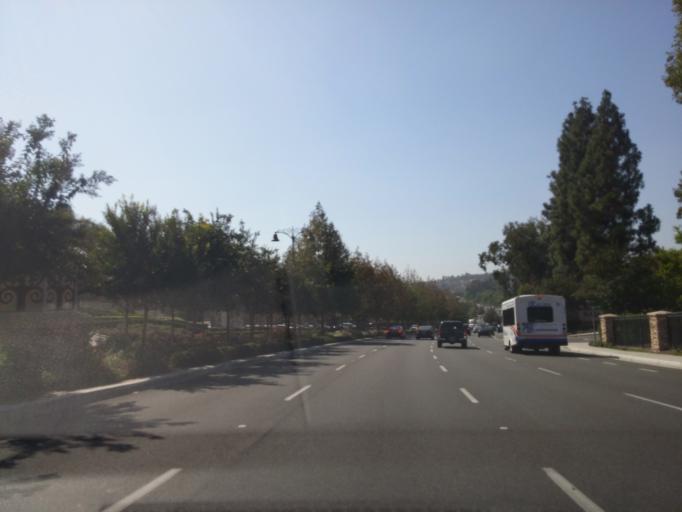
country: US
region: California
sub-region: Orange County
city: Mission Viejo
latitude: 33.5835
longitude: -117.6608
